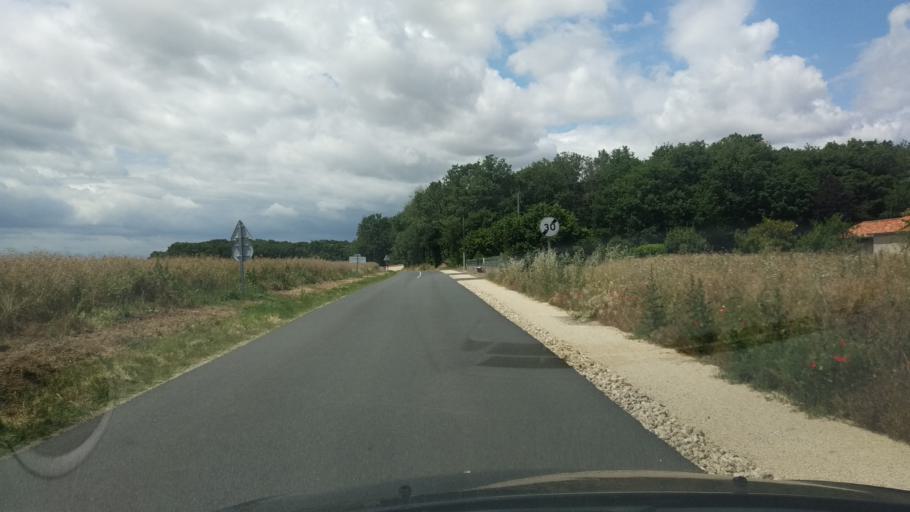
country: FR
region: Poitou-Charentes
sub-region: Departement de la Vienne
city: Cisse
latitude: 46.6115
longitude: 0.2271
